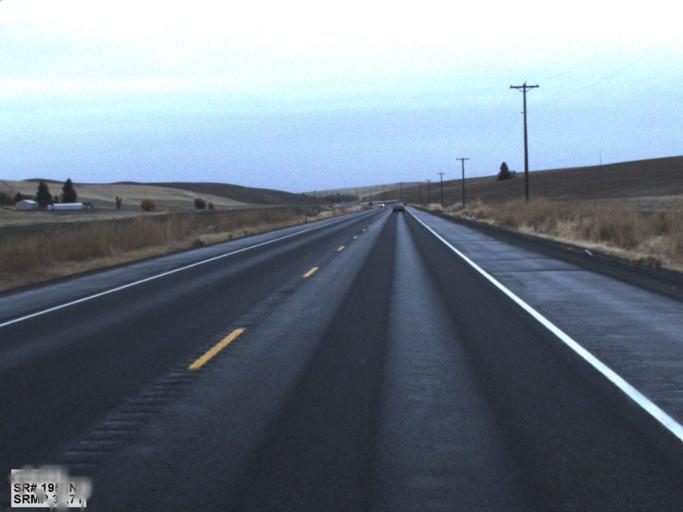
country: US
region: Washington
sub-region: Whitman County
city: Colfax
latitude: 46.8067
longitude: -117.3181
